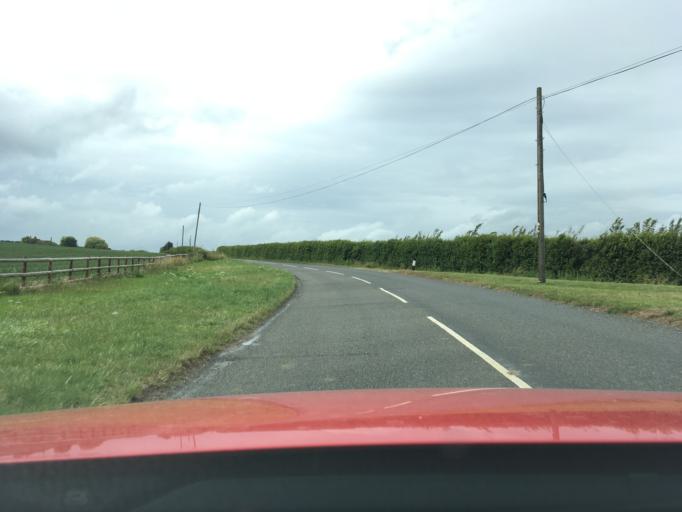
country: GB
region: England
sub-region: Worcestershire
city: Badsey
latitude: 52.0520
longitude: -1.9197
